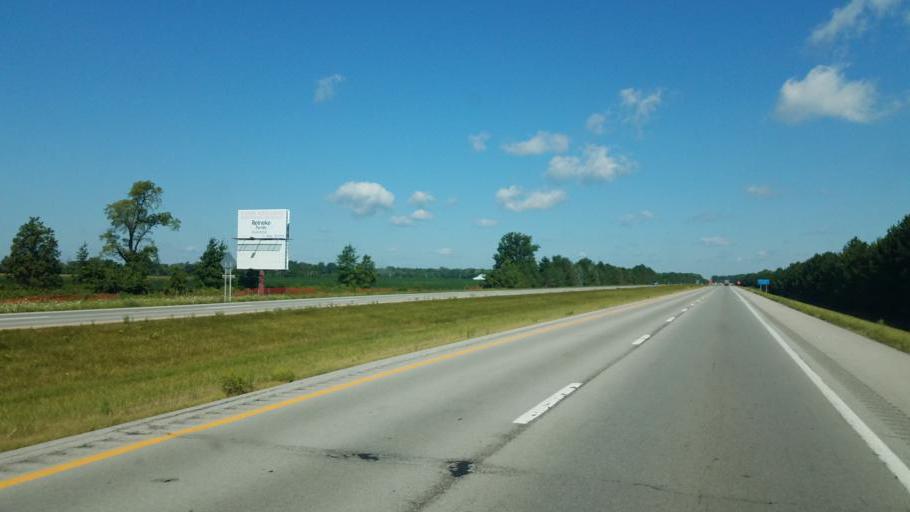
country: US
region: Ohio
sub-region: Wyandot County
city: Carey
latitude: 40.9038
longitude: -83.3465
